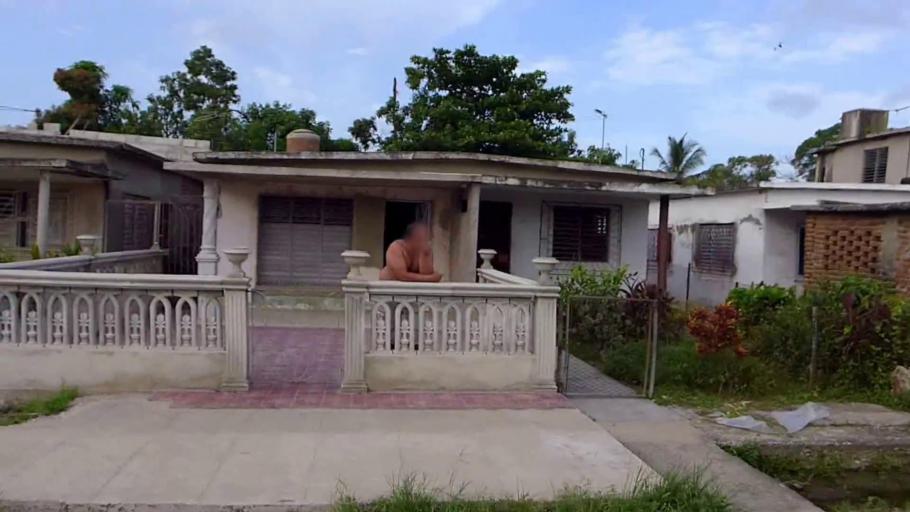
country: CU
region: Camaguey
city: Camaguey
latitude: 21.3819
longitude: -77.9417
